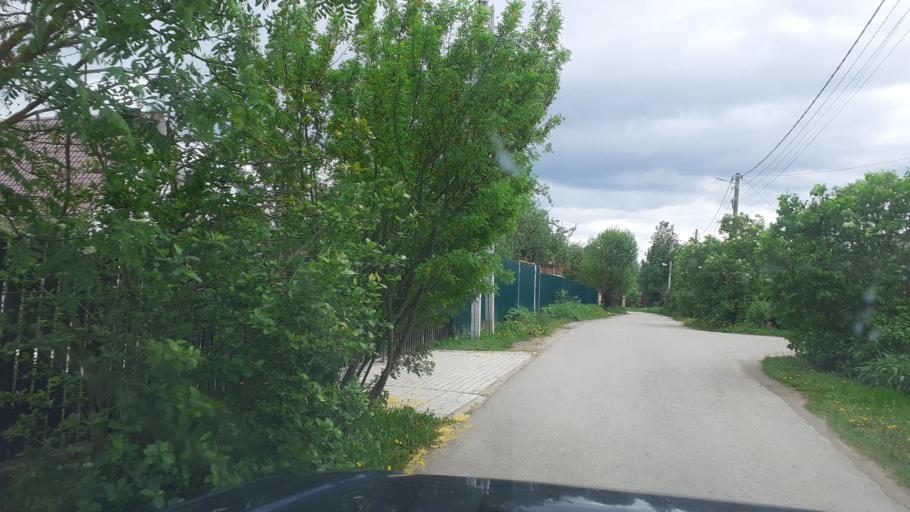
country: RU
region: Moskovskaya
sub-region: Volokolamskiy Rayon
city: Volokolamsk
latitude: 56.0381
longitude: 35.9444
